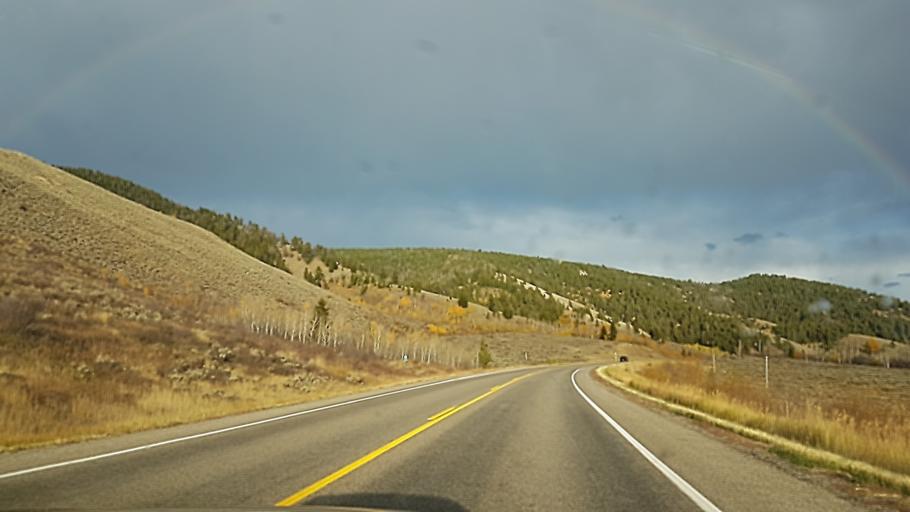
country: US
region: Montana
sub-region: Gallatin County
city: West Yellowstone
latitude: 44.6631
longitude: -111.3710
